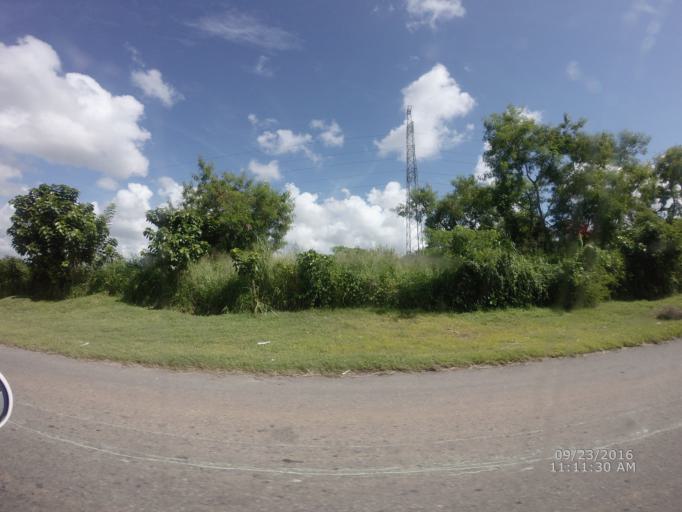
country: CU
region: La Habana
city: Arroyo Naranjo
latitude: 23.0256
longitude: -82.2702
